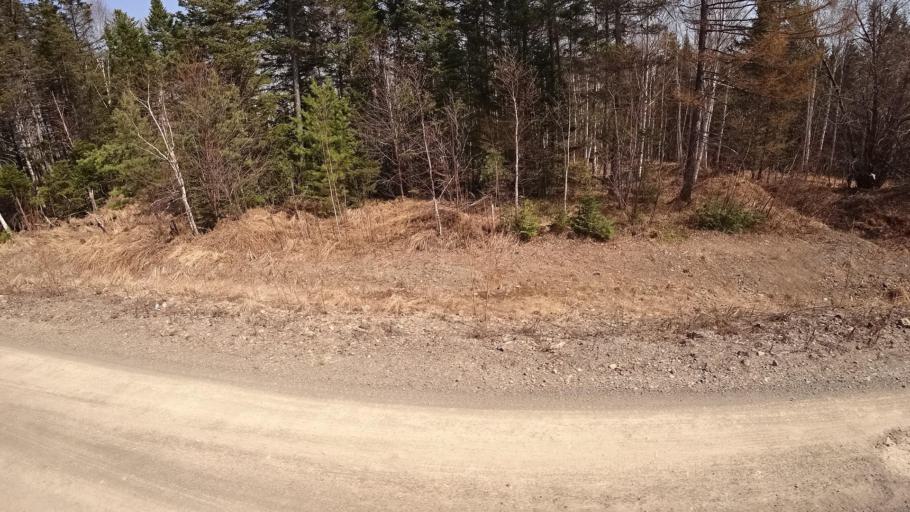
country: RU
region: Khabarovsk Krai
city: Selikhino
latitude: 50.6227
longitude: 137.3996
